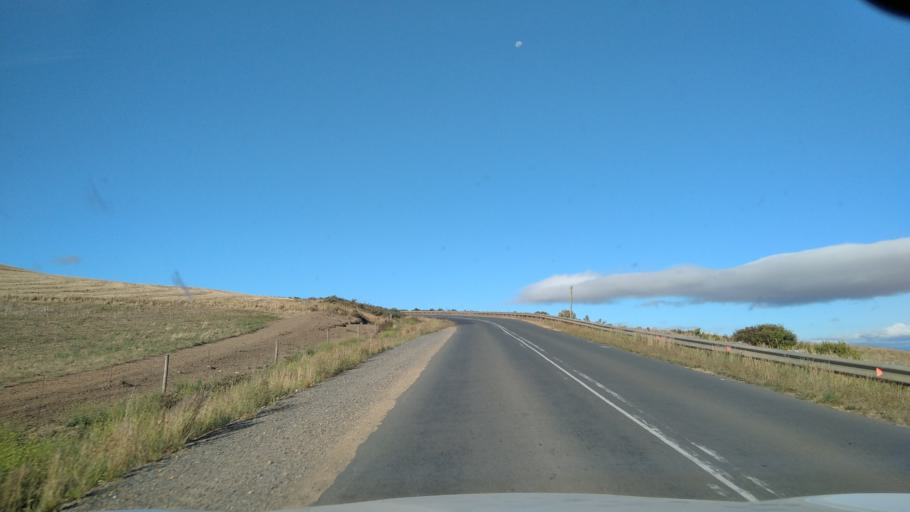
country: ZA
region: Western Cape
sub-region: Overberg District Municipality
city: Caledon
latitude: -34.1596
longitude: 19.3040
